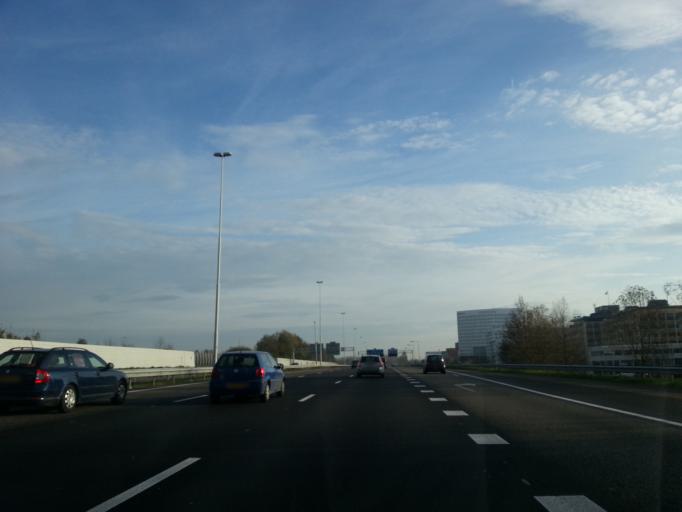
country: NL
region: South Holland
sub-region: Gemeente Rotterdam
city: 's-Gravenland
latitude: 51.9532
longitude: 4.5481
